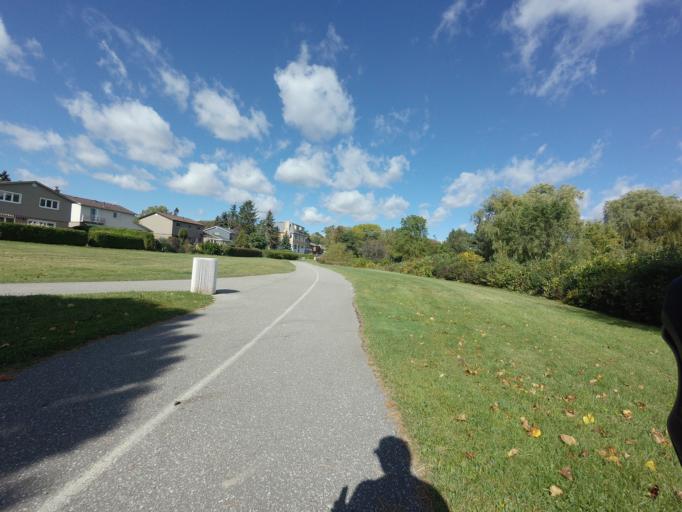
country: CA
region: Ontario
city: Ajax
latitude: 43.8166
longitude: -79.0980
